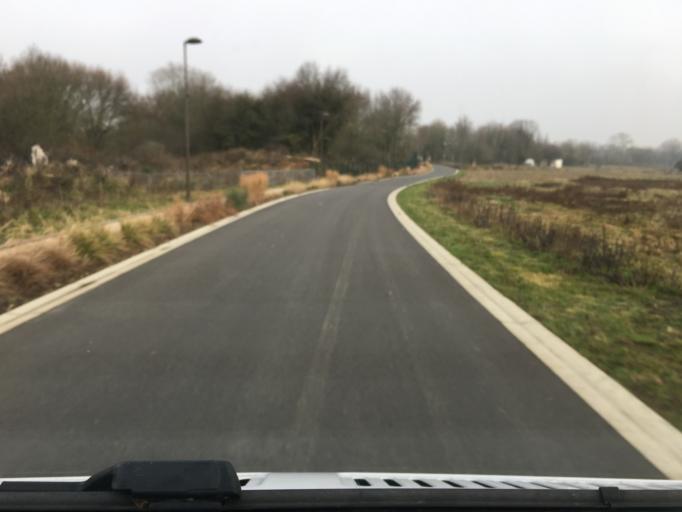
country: FR
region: Picardie
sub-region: Departement de la Somme
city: Saint-Valery-sur-Somme
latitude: 50.1756
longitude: 1.6287
